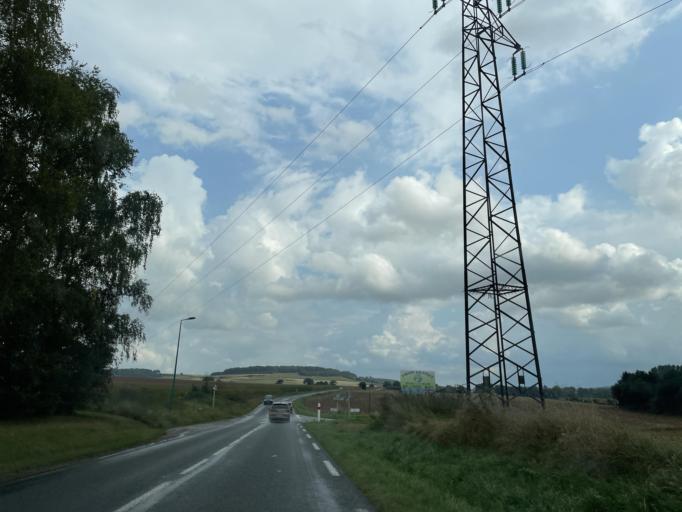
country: FR
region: Haute-Normandie
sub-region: Departement de la Seine-Maritime
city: Envermeu
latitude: 49.8831
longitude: 1.2949
